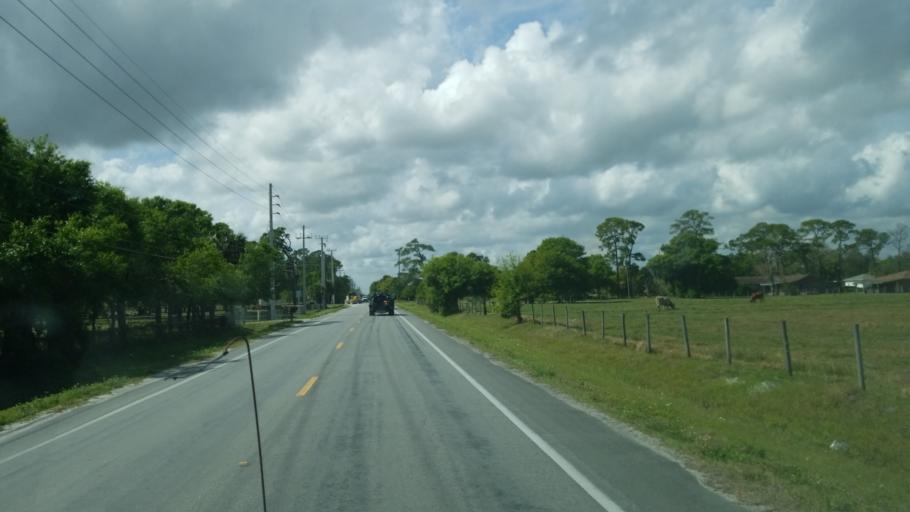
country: US
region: Florida
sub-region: Saint Lucie County
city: Lakewood Park
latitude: 27.4477
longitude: -80.4463
